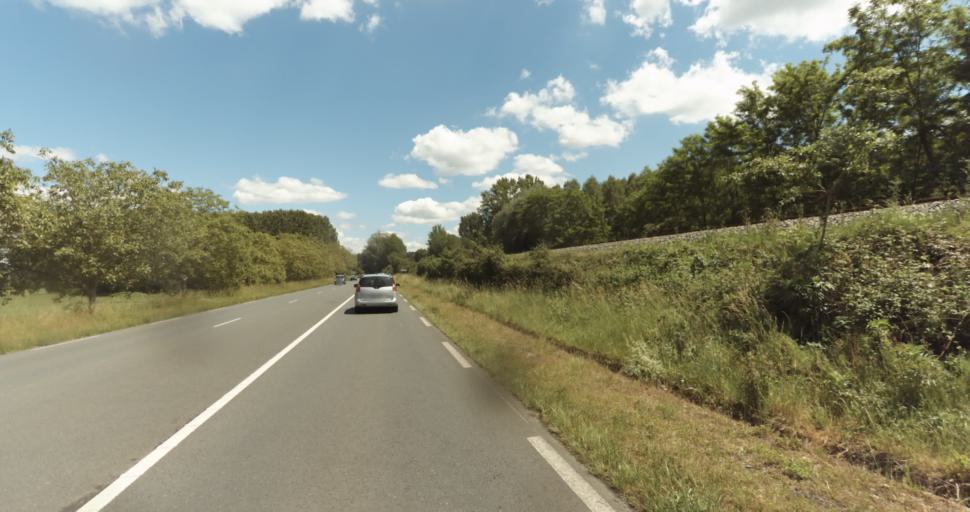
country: FR
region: Aquitaine
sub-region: Departement de la Dordogne
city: Belves
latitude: 44.8223
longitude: 0.9626
